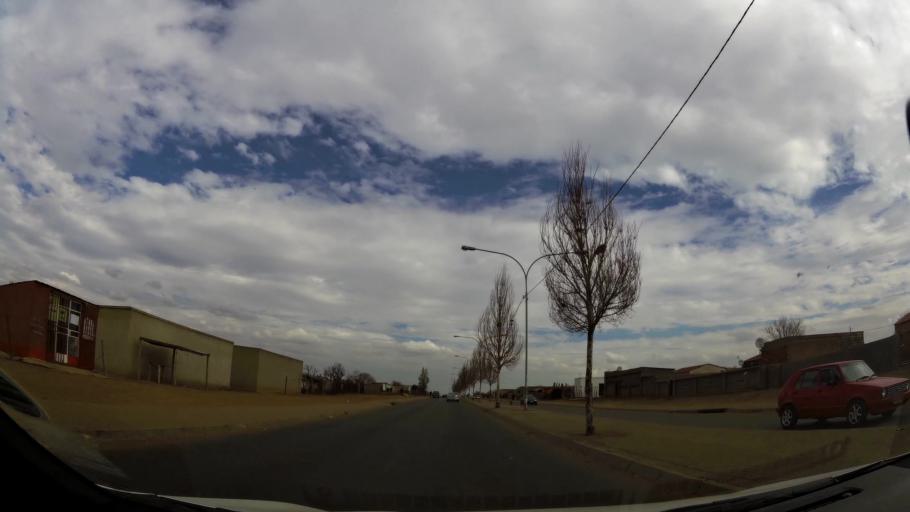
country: ZA
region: Gauteng
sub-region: Ekurhuleni Metropolitan Municipality
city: Germiston
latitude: -26.3983
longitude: 28.1570
